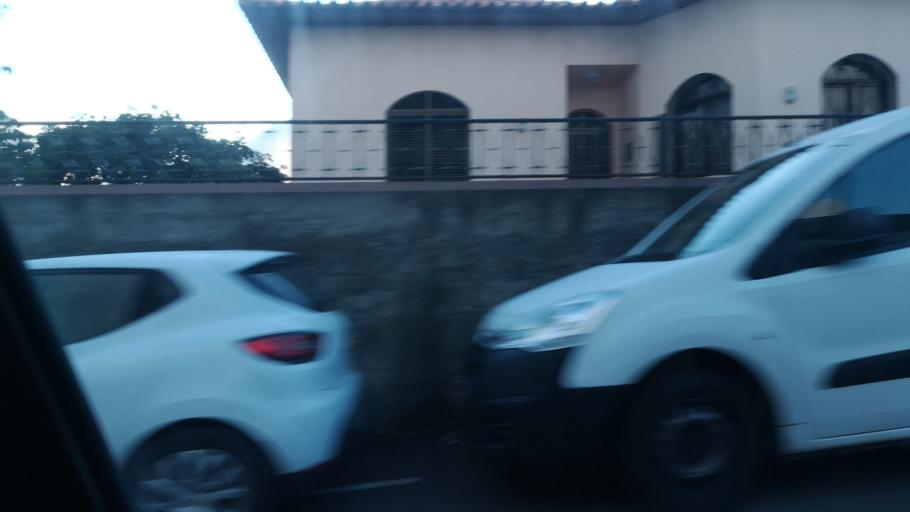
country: PT
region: Madeira
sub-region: Santa Cruz
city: Camacha
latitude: 32.6745
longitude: -16.8240
